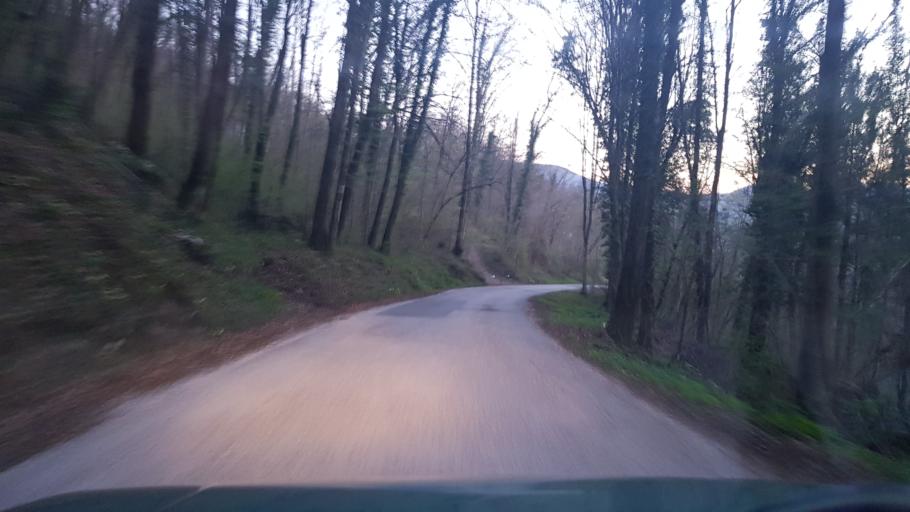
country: SI
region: Kanal
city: Kanal
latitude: 46.0745
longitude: 13.6374
